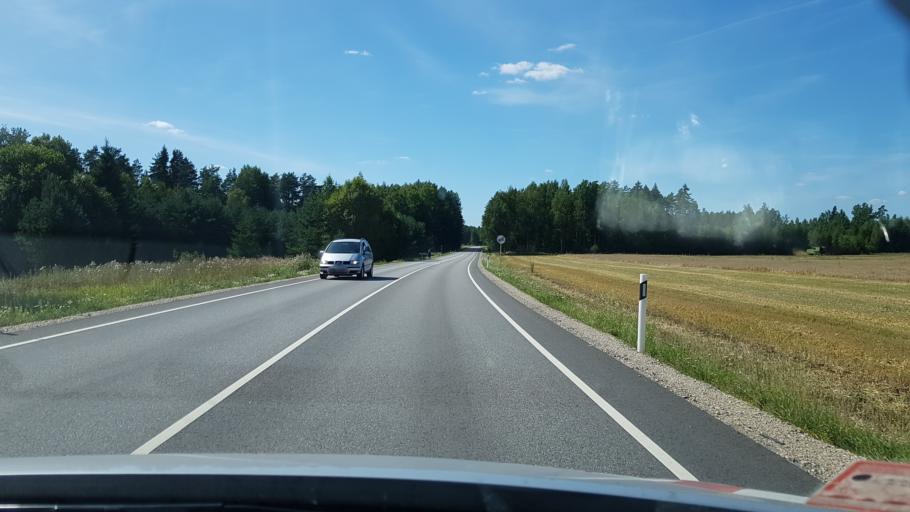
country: EE
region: Polvamaa
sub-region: Polva linn
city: Polva
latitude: 58.0040
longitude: 27.2244
